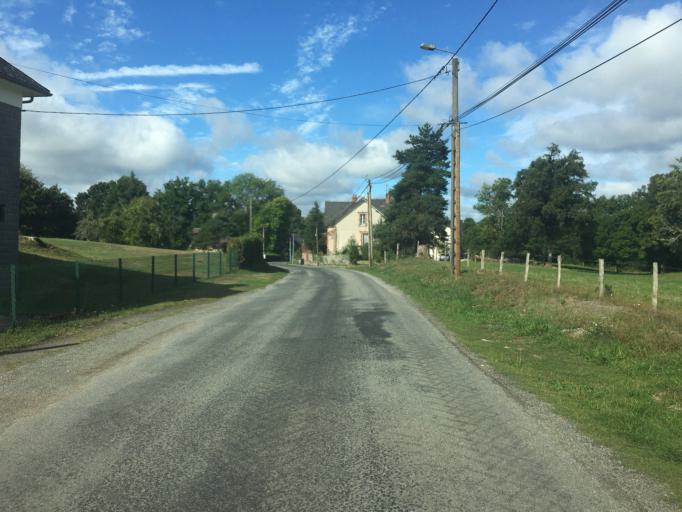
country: FR
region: Auvergne
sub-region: Departement du Cantal
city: Champagnac
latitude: 45.4157
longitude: 2.4099
